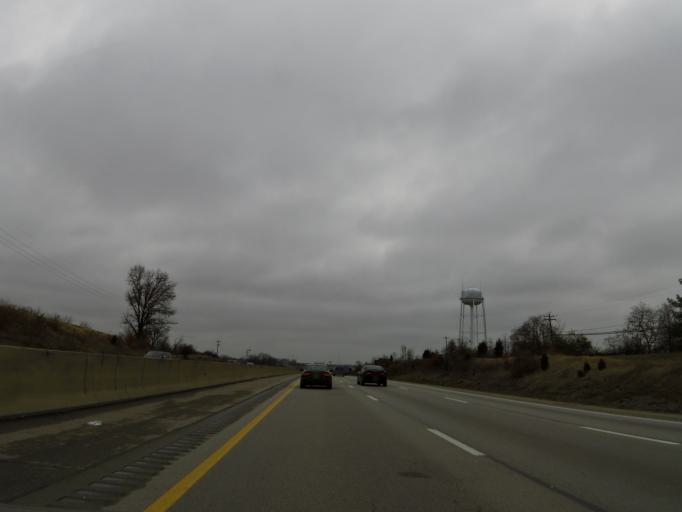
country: US
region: Kentucky
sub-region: Boone County
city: Walton
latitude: 38.8695
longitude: -84.6242
